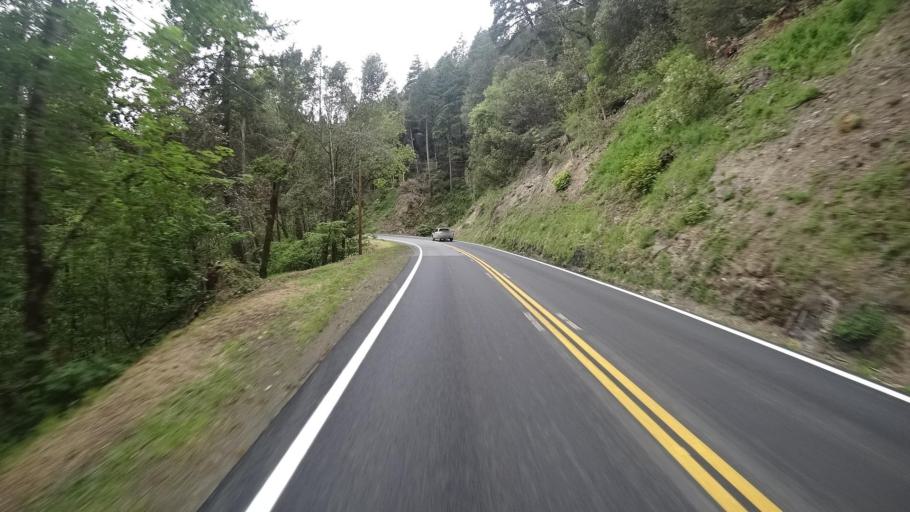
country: US
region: California
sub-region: Humboldt County
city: Willow Creek
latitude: 41.0095
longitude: -123.6463
